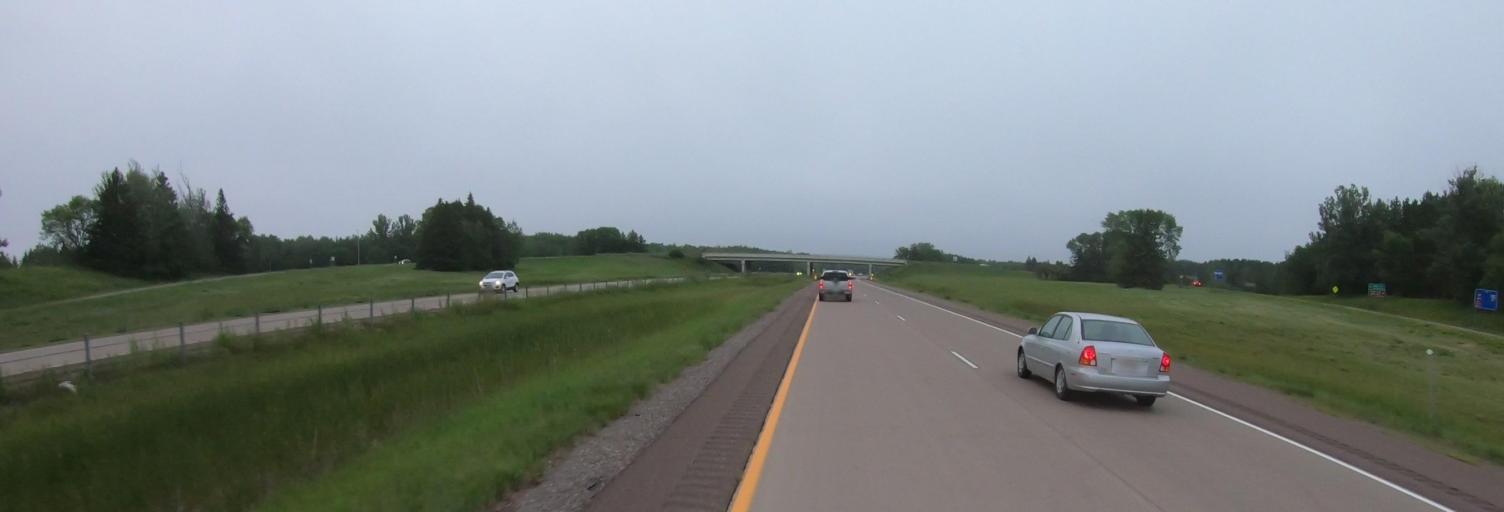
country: US
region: Minnesota
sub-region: Carlton County
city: Moose Lake
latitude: 46.4338
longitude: -92.7464
